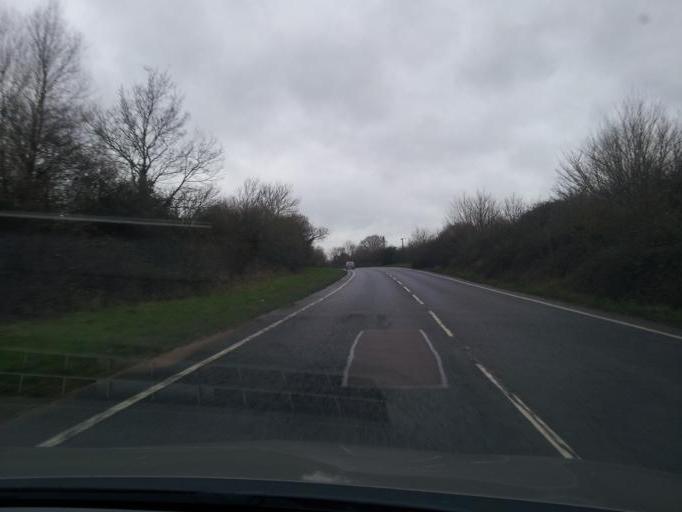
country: GB
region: England
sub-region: Norfolk
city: Diss
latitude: 52.3543
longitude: 1.0967
